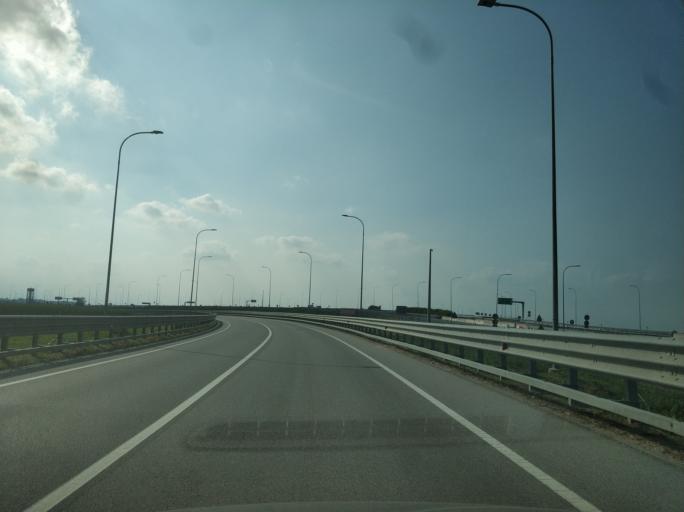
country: IT
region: Piedmont
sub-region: Provincia di Cuneo
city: Roreto
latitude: 44.6630
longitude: 7.8121
